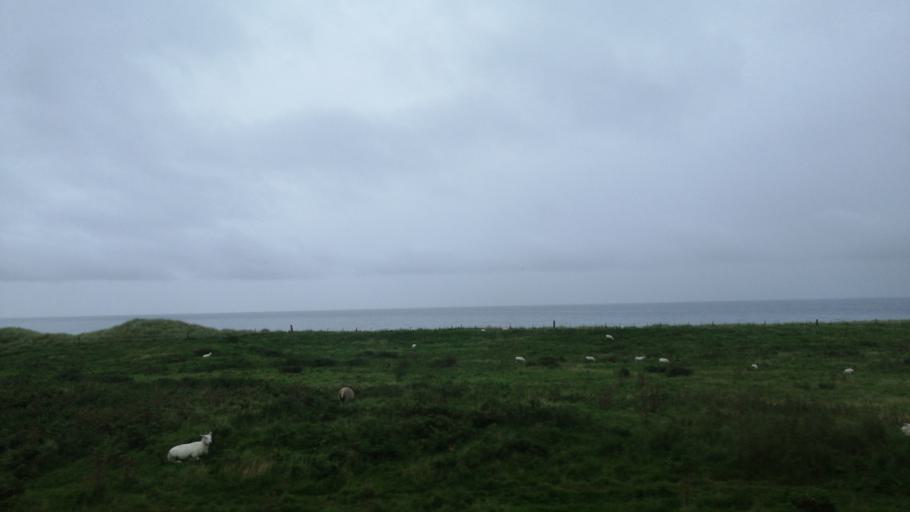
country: GB
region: Scotland
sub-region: Highland
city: Brora
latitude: 58.0469
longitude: -3.8168
